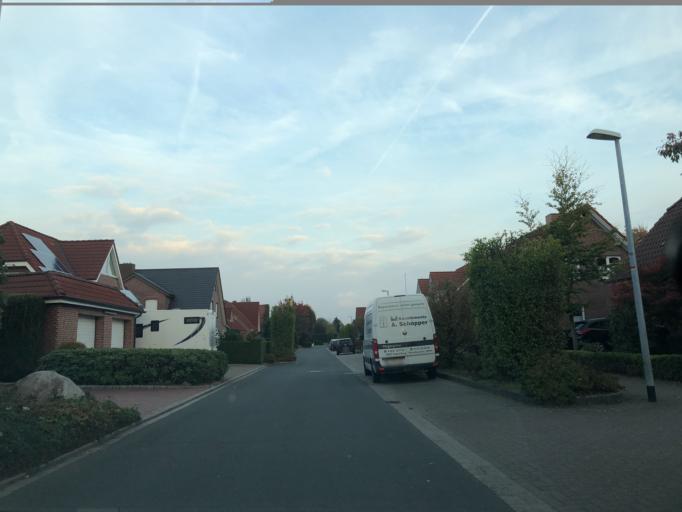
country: DE
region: Lower Saxony
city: Papenburg
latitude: 53.0754
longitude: 7.4283
